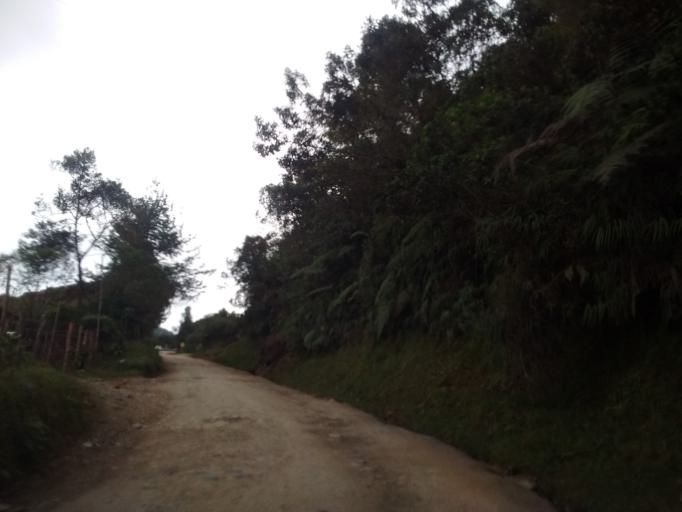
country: CO
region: Huila
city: Isnos
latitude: 2.0338
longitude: -76.2762
